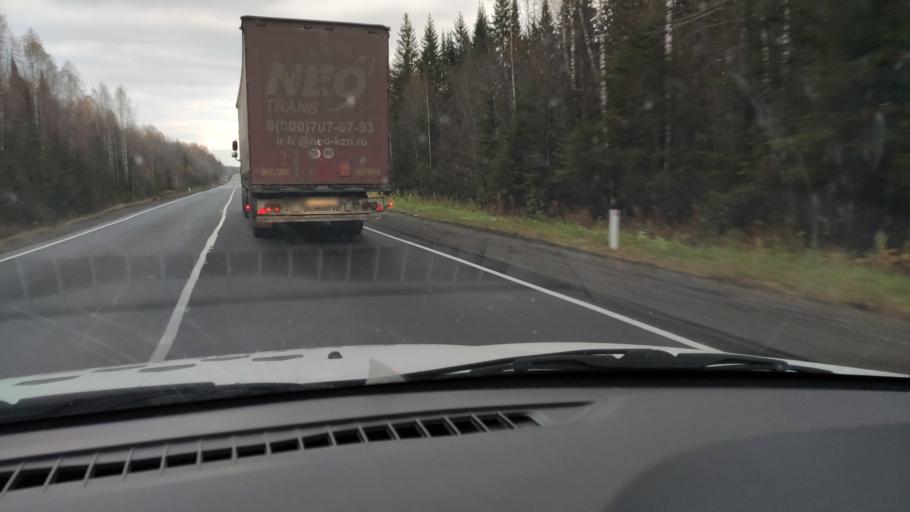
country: RU
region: Kirov
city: Omutninsk
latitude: 58.7603
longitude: 52.0116
